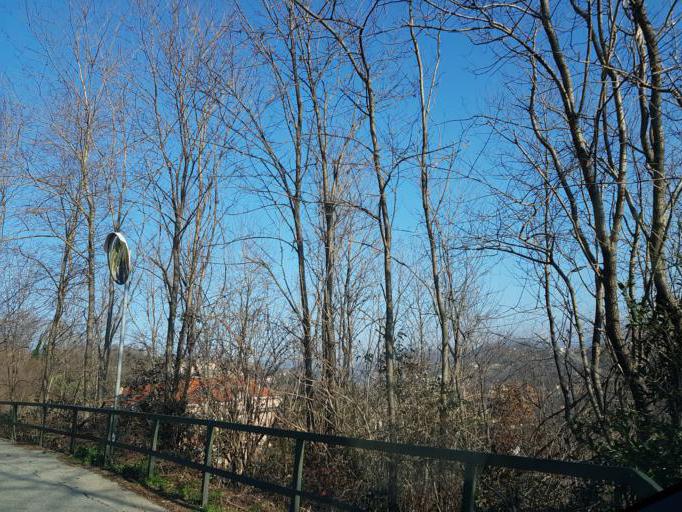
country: IT
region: Liguria
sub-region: Provincia di Genova
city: Santa Marta
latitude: 44.4860
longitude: 8.8949
